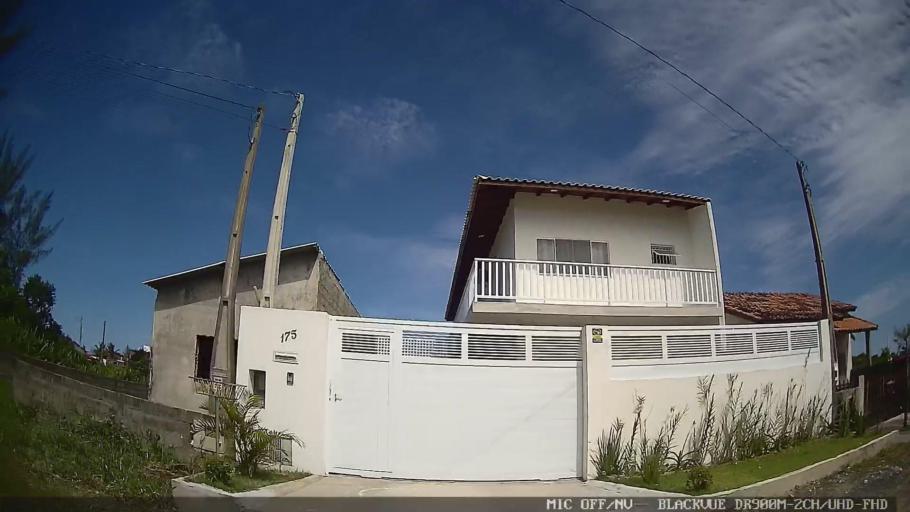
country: BR
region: Sao Paulo
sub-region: Iguape
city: Iguape
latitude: -24.7908
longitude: -47.6183
